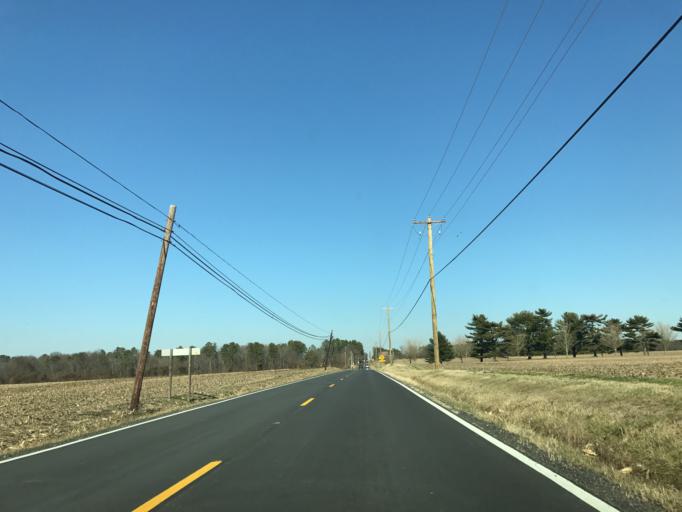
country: US
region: Maryland
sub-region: Queen Anne's County
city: Grasonville
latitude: 38.9960
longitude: -76.1412
